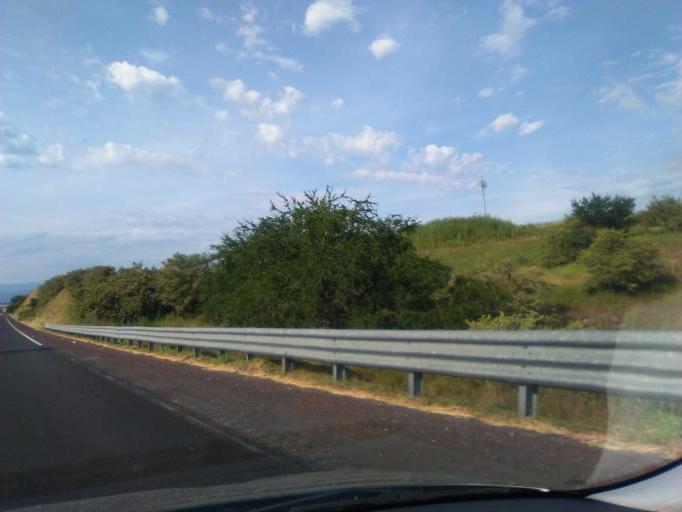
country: MX
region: Morelos
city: Puente de Ixtla
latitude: 18.6106
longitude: -99.2881
